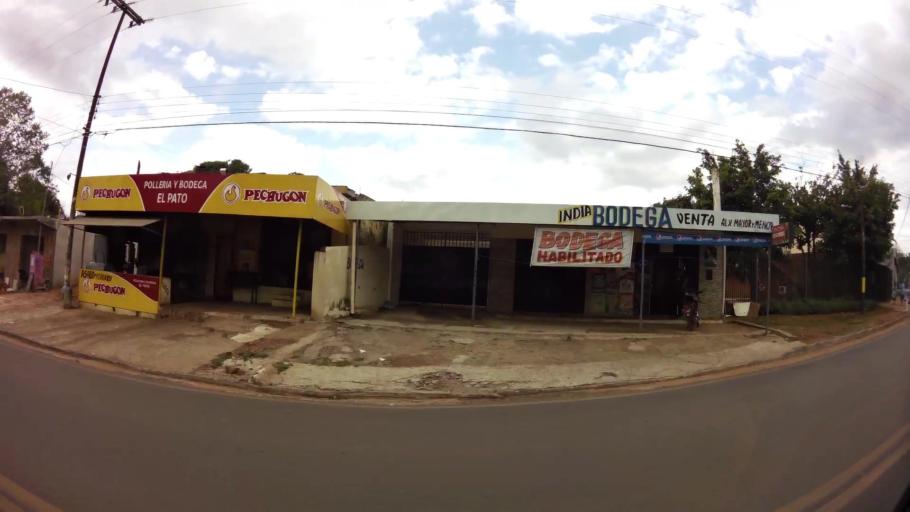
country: PY
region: Central
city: San Lorenzo
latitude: -25.2901
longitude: -57.4824
